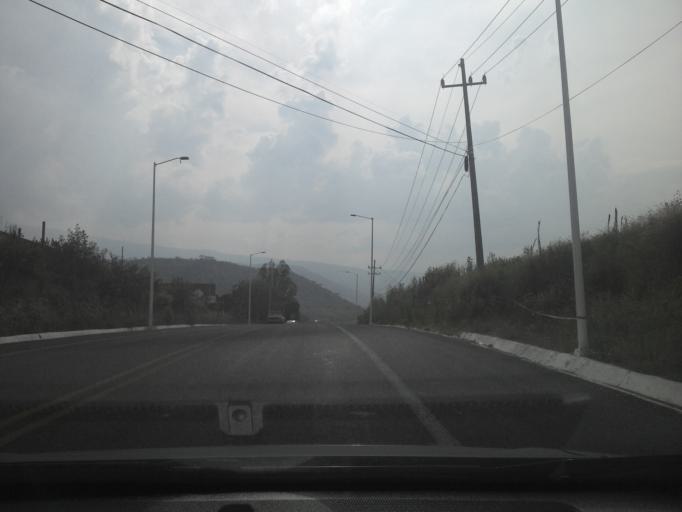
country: MX
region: Jalisco
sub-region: Tlajomulco de Zuniga
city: Lomas del Sur
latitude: 20.4864
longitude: -103.4270
